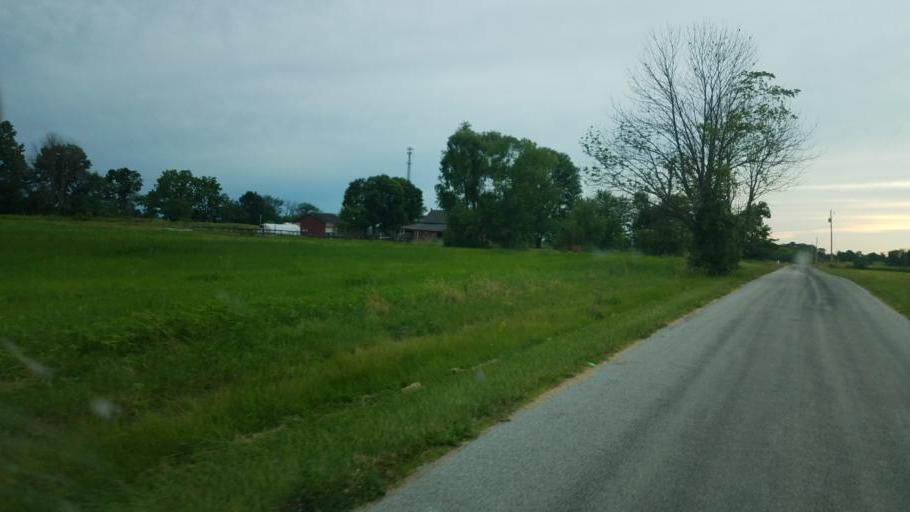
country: US
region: Ohio
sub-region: Huron County
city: Greenwich
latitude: 40.9167
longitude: -82.4911
